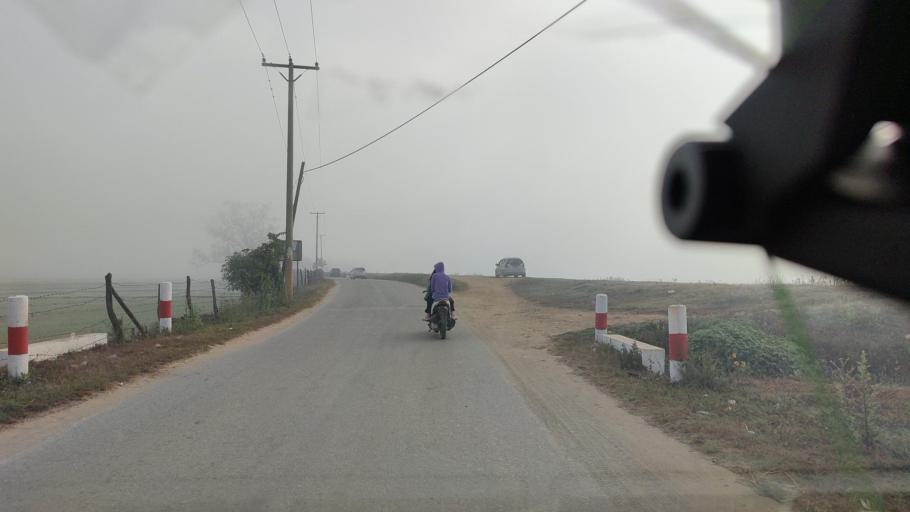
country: MM
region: Shan
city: Taunggyi
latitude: 21.2781
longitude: 97.6715
